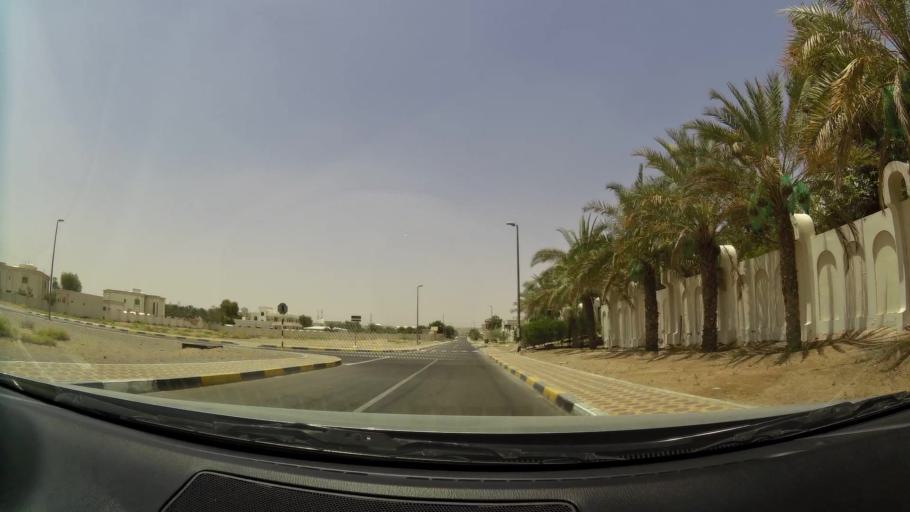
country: OM
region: Al Buraimi
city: Al Buraymi
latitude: 24.2650
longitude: 55.7133
